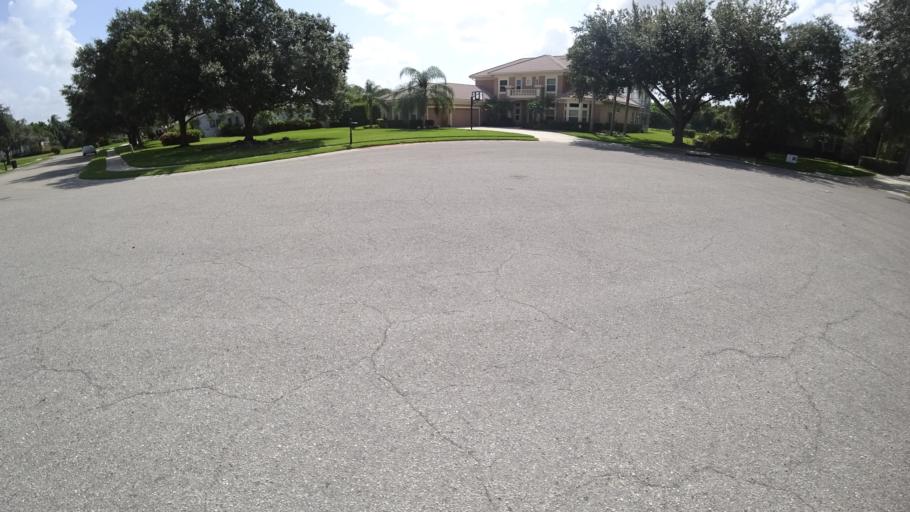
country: US
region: Florida
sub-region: Sarasota County
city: The Meadows
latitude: 27.4074
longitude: -82.4449
